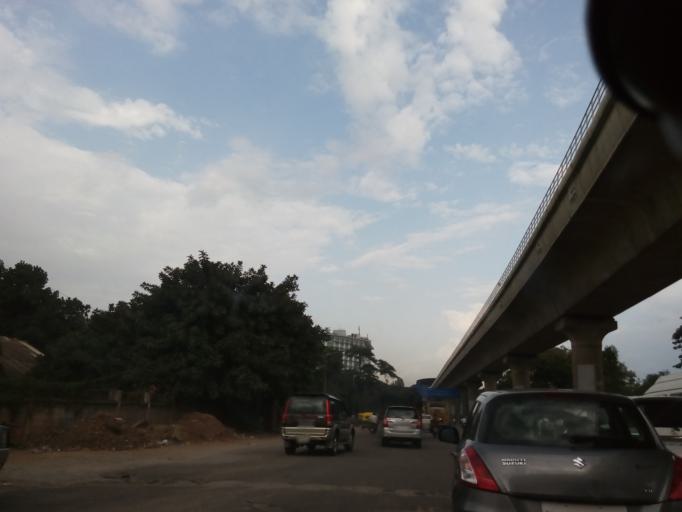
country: IN
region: Karnataka
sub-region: Bangalore Urban
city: Bangalore
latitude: 13.0304
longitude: 77.5375
